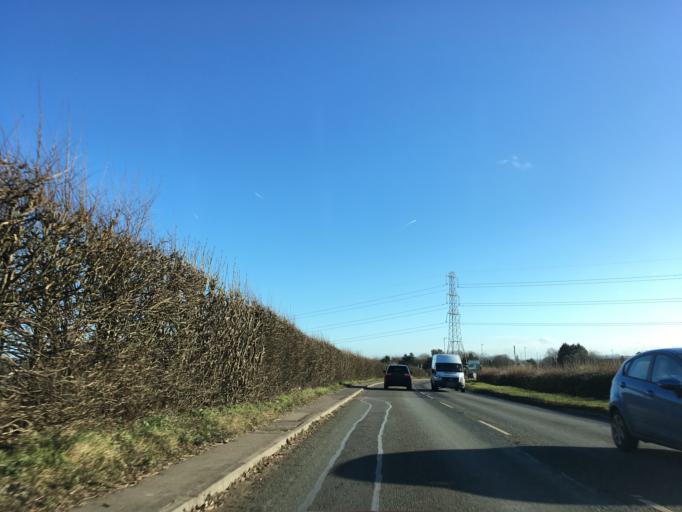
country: GB
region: England
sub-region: Wiltshire
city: Chippenham
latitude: 51.4699
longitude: -2.1469
